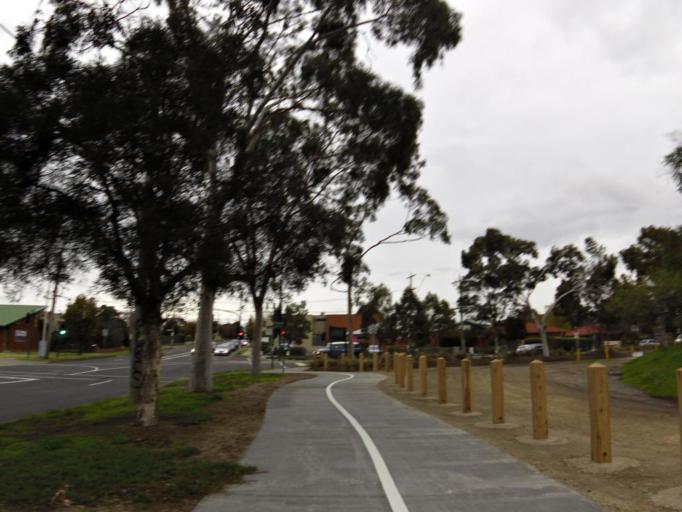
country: AU
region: Victoria
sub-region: Whitehorse
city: Box Hill North
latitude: -37.7995
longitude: 145.1180
